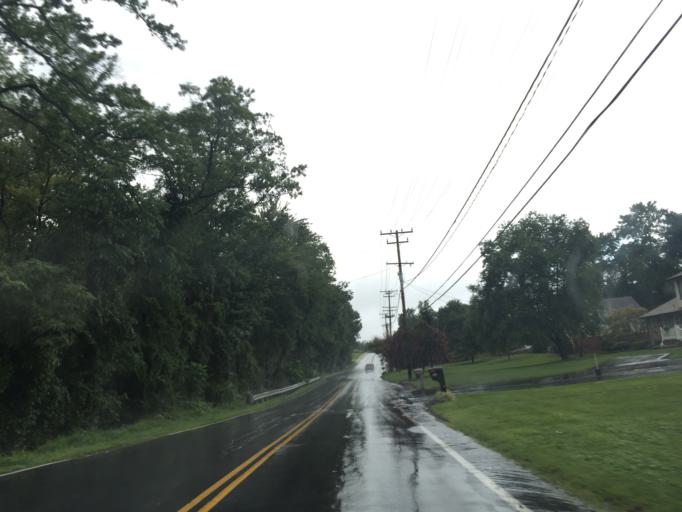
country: US
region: Maryland
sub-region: Harford County
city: Riverside
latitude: 39.4635
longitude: -76.2816
